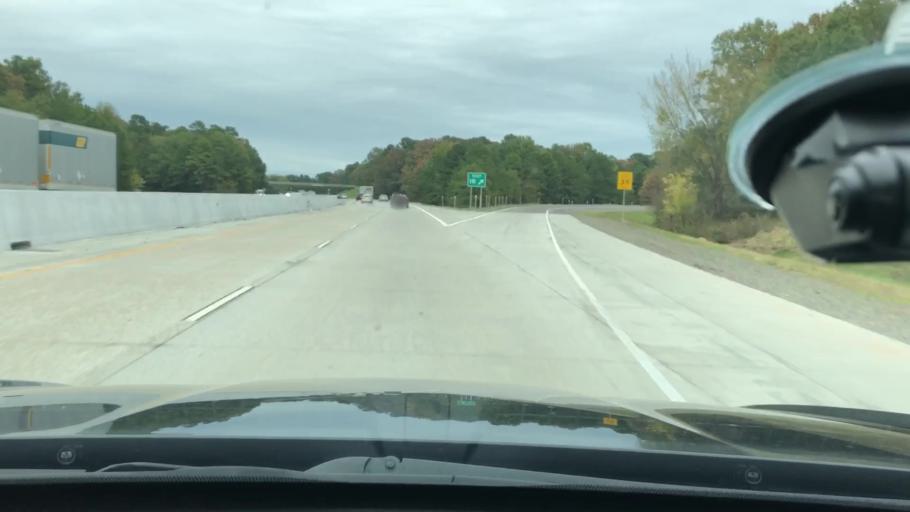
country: US
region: Arkansas
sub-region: Hempstead County
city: Hope
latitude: 33.6088
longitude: -93.8032
